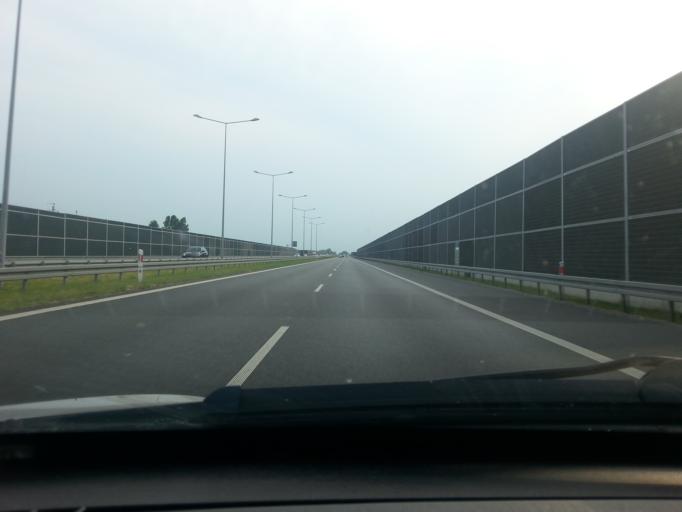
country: PL
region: Masovian Voivodeship
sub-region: Powiat zyrardowski
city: Zyrardow
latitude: 52.1080
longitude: 20.4520
